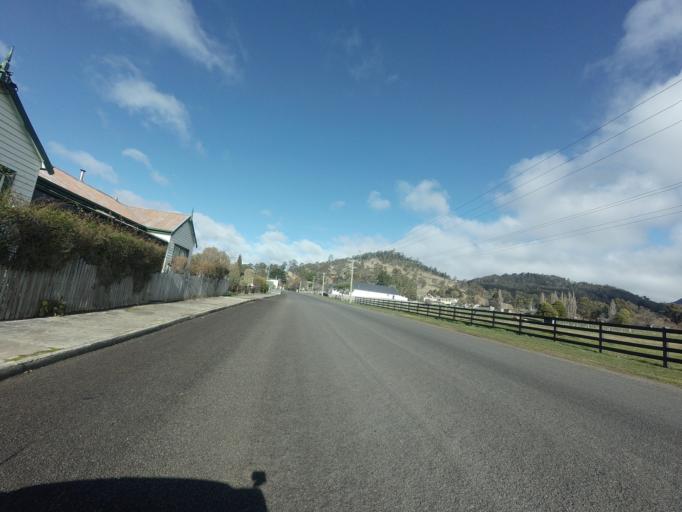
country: AU
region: Tasmania
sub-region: Derwent Valley
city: New Norfolk
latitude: -42.6171
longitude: 146.7160
